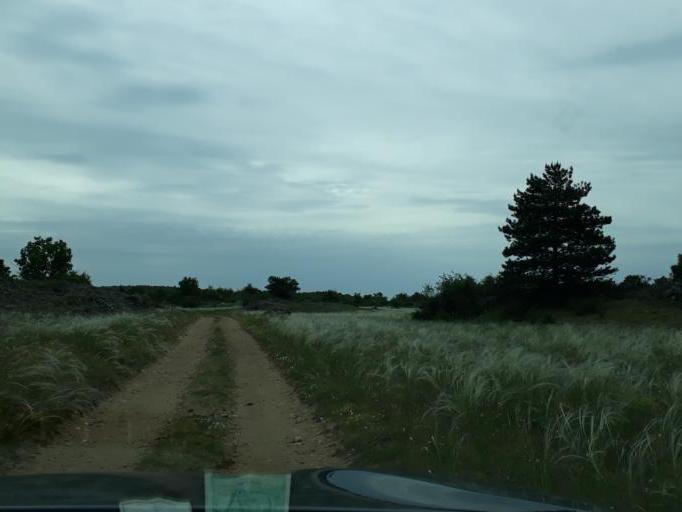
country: FR
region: Languedoc-Roussillon
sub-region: Departement de l'Herault
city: Lodeve
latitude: 43.8173
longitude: 3.2782
